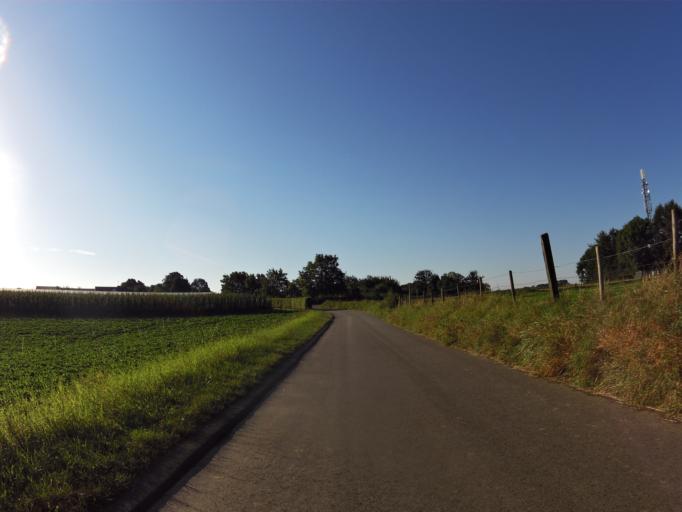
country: NL
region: Limburg
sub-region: Gemeente Voerendaal
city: Klimmen
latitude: 50.8687
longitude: 5.8973
